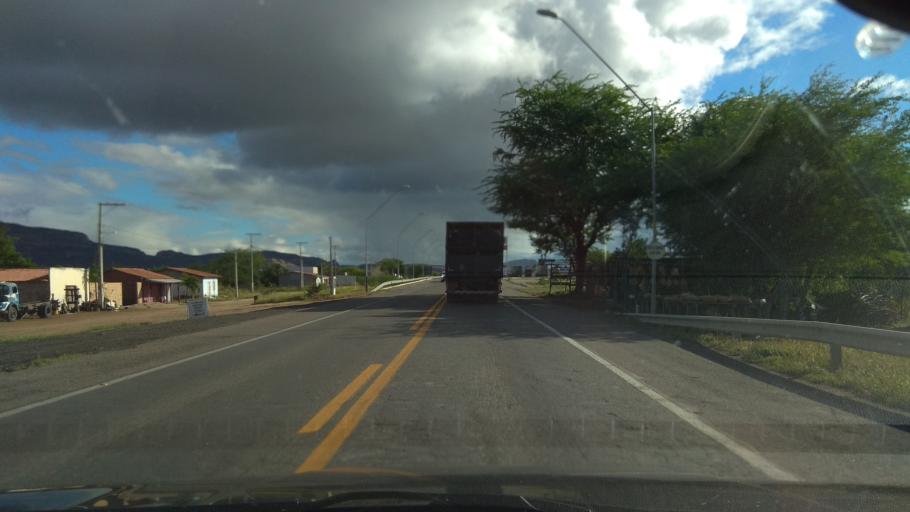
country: BR
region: Bahia
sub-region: Castro Alves
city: Castro Alves
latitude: -12.6966
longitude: -39.7045
